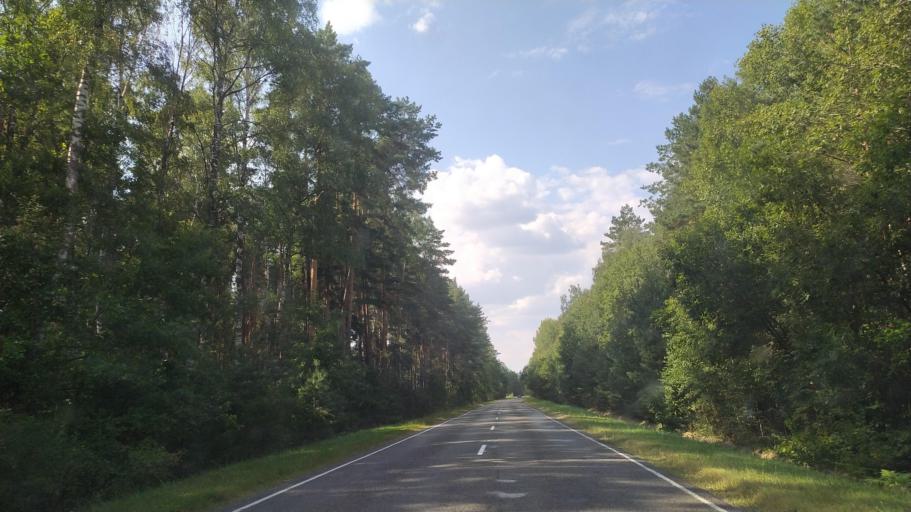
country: BY
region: Brest
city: Drahichyn
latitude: 52.3111
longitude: 25.0392
